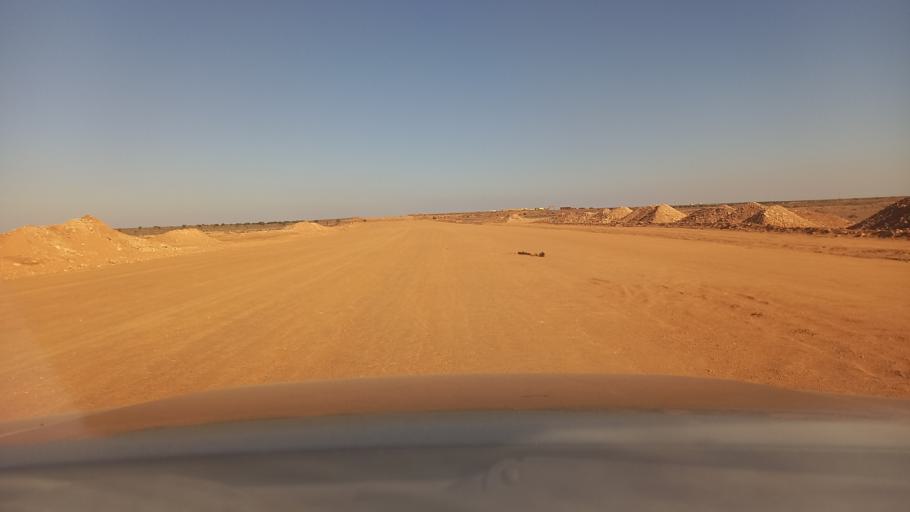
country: TN
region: Madanin
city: Medenine
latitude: 33.1695
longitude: 10.5256
